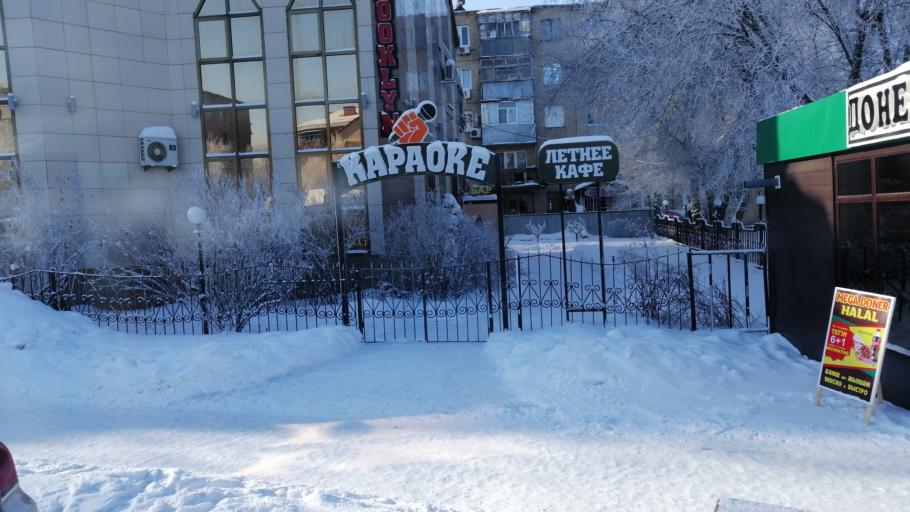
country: KZ
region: Aqtoebe
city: Aqtobe
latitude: 50.3066
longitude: 57.1498
